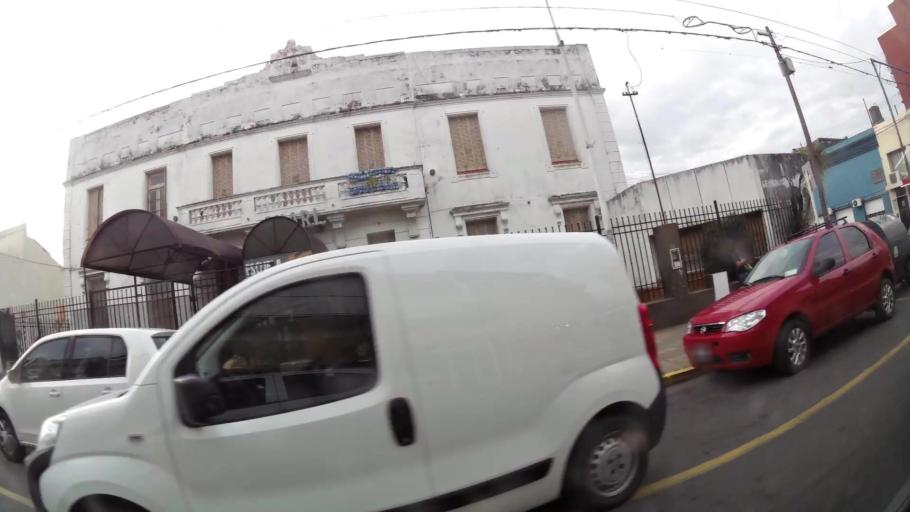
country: AR
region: Buenos Aires
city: San Nicolas de los Arroyos
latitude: -33.3354
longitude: -60.2216
